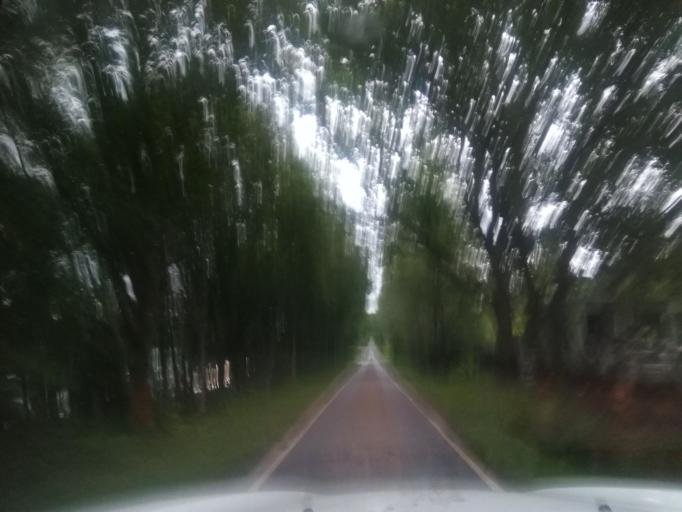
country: GB
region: Scotland
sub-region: Highland
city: Fort William
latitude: 56.8469
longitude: -5.2961
